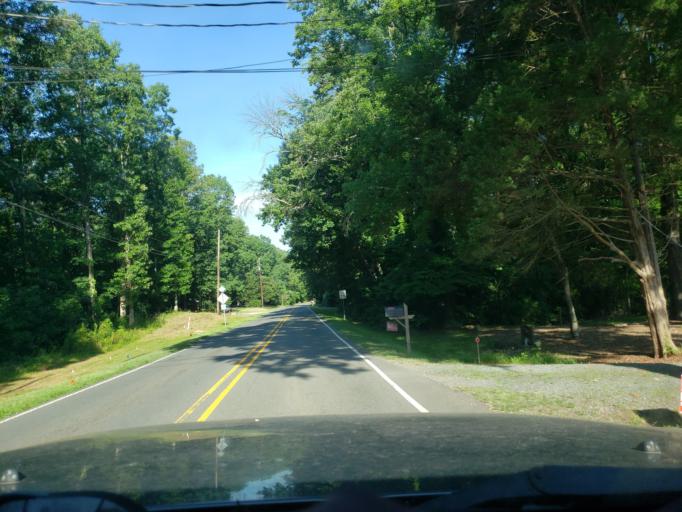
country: US
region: North Carolina
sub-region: Durham County
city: Durham
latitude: 35.9560
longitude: -78.8598
